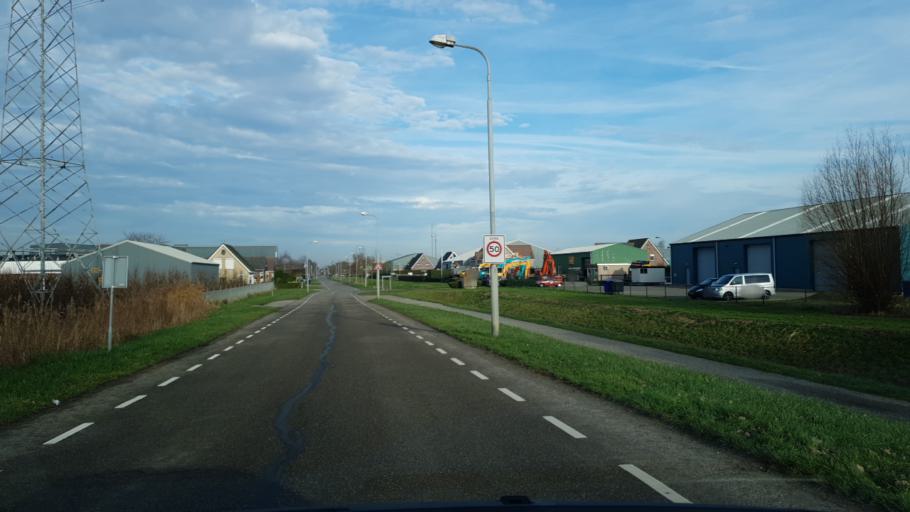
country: NL
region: Zeeland
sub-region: Gemeente Reimerswaal
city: Yerseke
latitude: 51.4207
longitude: 4.1090
